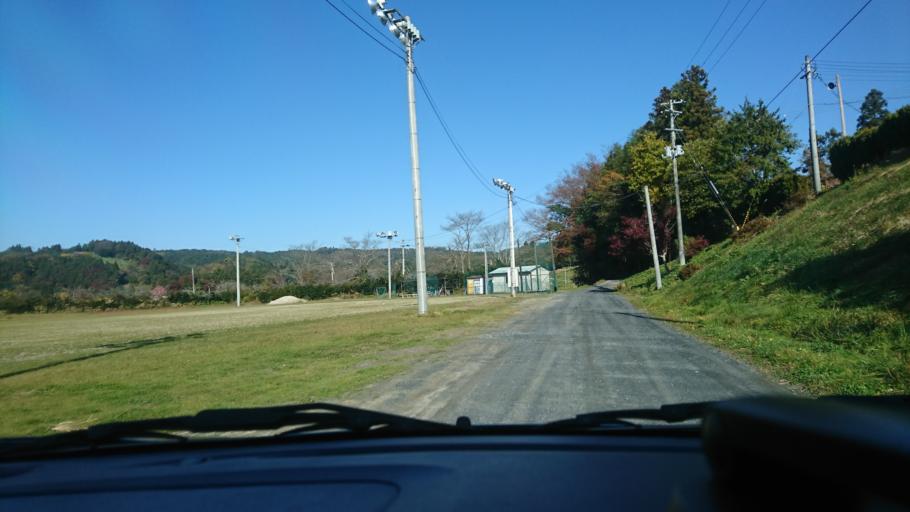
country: JP
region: Iwate
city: Ichinoseki
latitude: 38.8517
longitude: 141.2887
